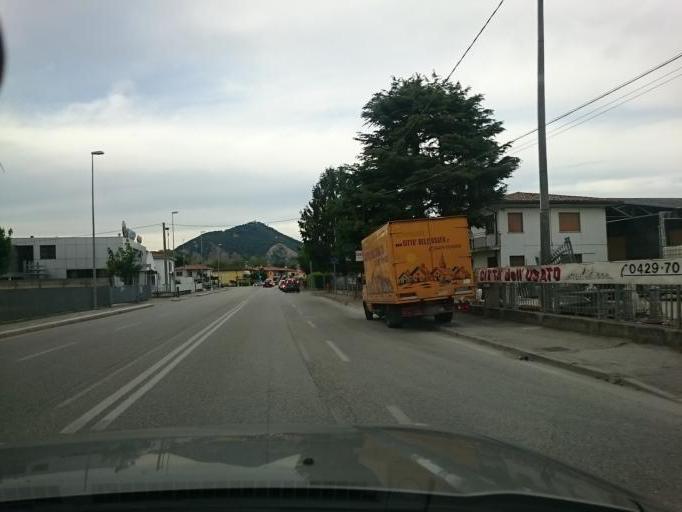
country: IT
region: Veneto
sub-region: Provincia di Padova
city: Monselice
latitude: 45.2290
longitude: 11.7453
